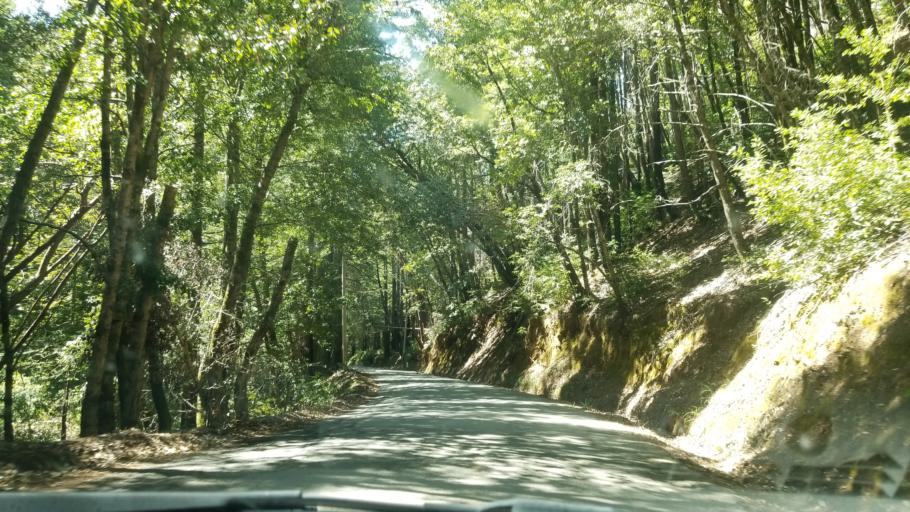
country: US
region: California
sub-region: Santa Cruz County
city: Day Valley
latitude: 37.0707
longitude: -121.8343
